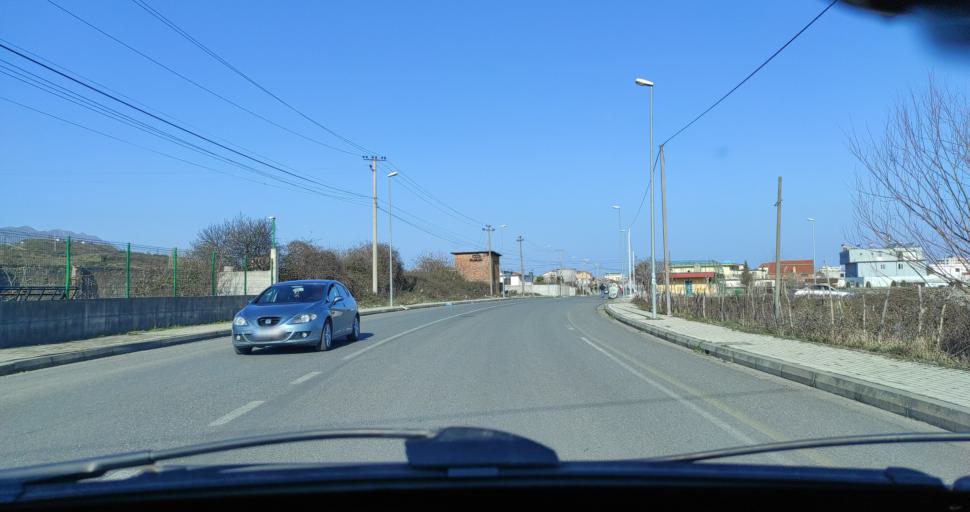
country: AL
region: Shkoder
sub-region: Rrethi i Malesia e Madhe
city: Kuc
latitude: 42.0540
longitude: 19.5196
